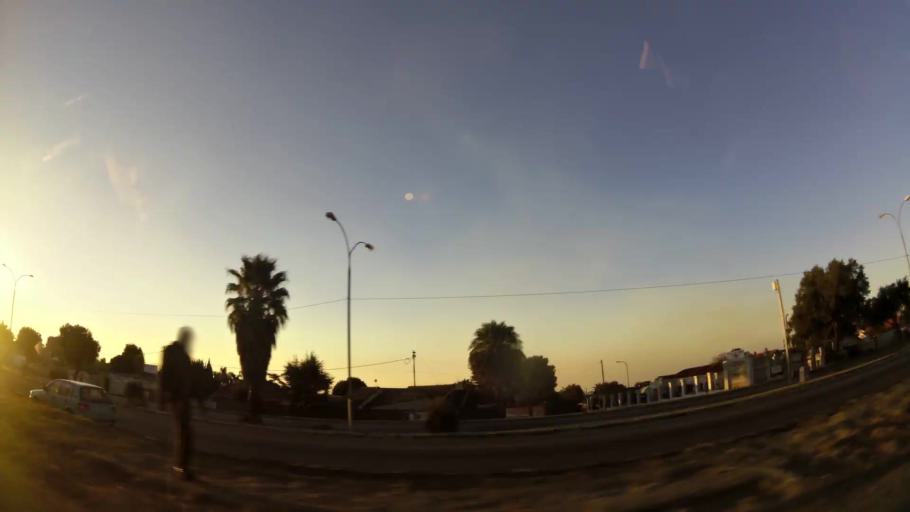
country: ZA
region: Gauteng
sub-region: City of Johannesburg Metropolitan Municipality
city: Roodepoort
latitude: -26.1466
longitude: 27.8847
